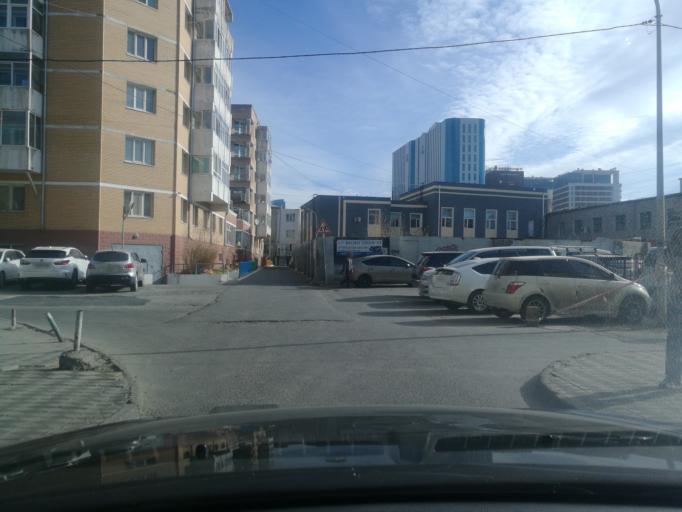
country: MN
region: Ulaanbaatar
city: Ulaanbaatar
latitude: 47.9146
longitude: 106.9072
